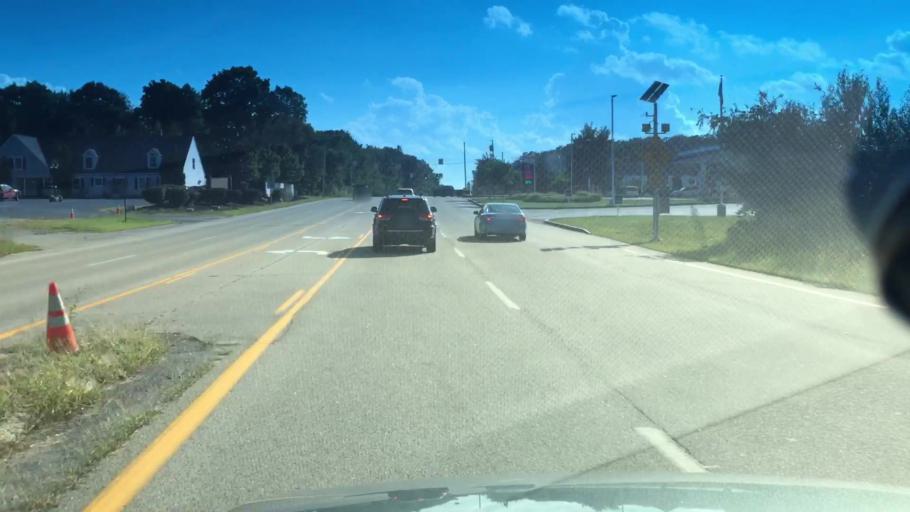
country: US
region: Maine
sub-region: York County
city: Kittery
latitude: 43.0998
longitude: -70.7466
